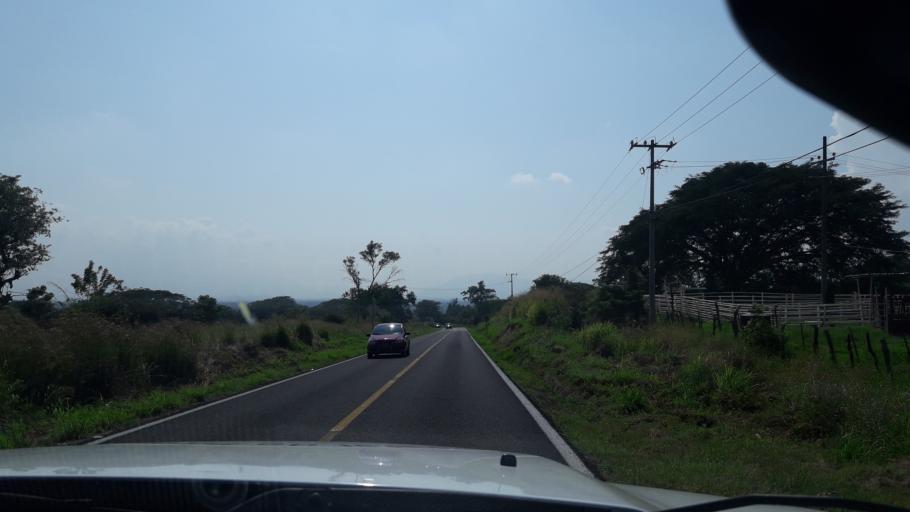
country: MX
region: Colima
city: Comala
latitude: 19.3410
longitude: -103.7434
